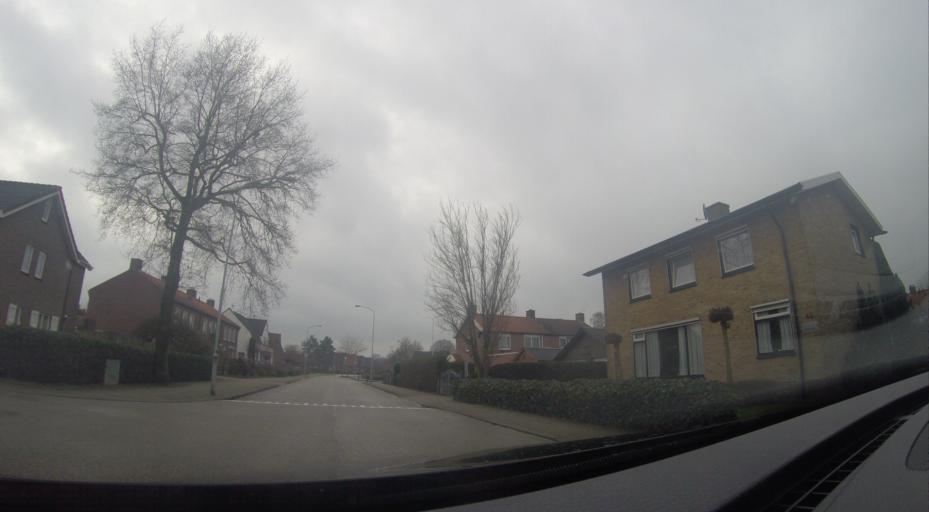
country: NL
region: Gelderland
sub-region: Gemeente Doetinchem
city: Doetinchem
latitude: 51.9641
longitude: 6.3106
